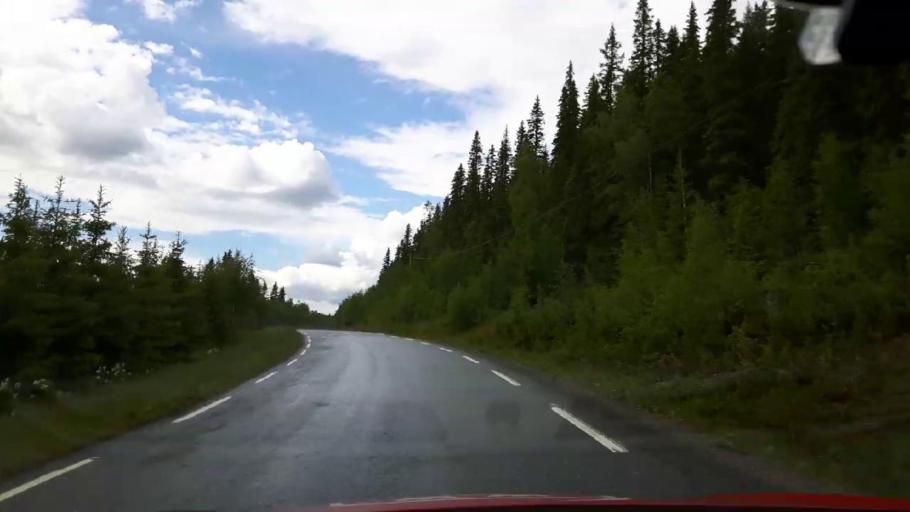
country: NO
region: Nord-Trondelag
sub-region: Lierne
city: Sandvika
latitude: 64.1034
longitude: 13.9984
